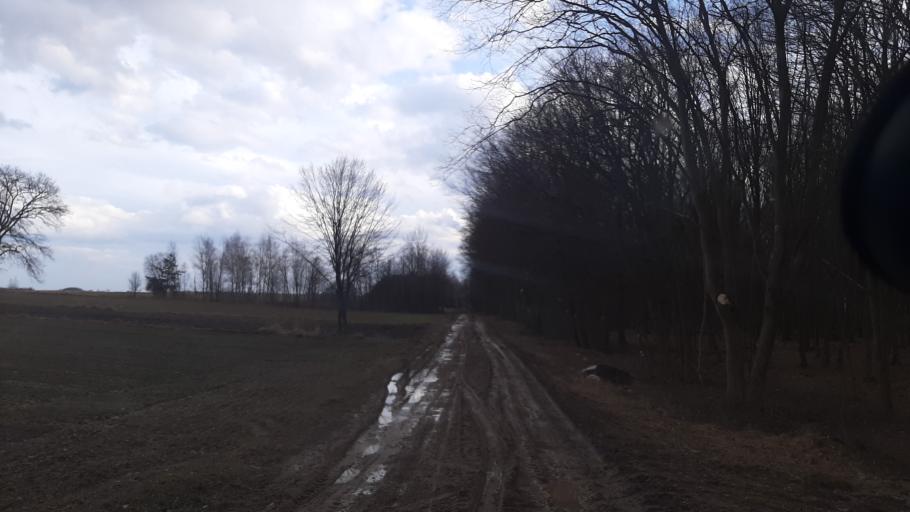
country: PL
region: Lublin Voivodeship
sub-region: Powiat lubelski
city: Jastkow
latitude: 51.3720
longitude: 22.4162
